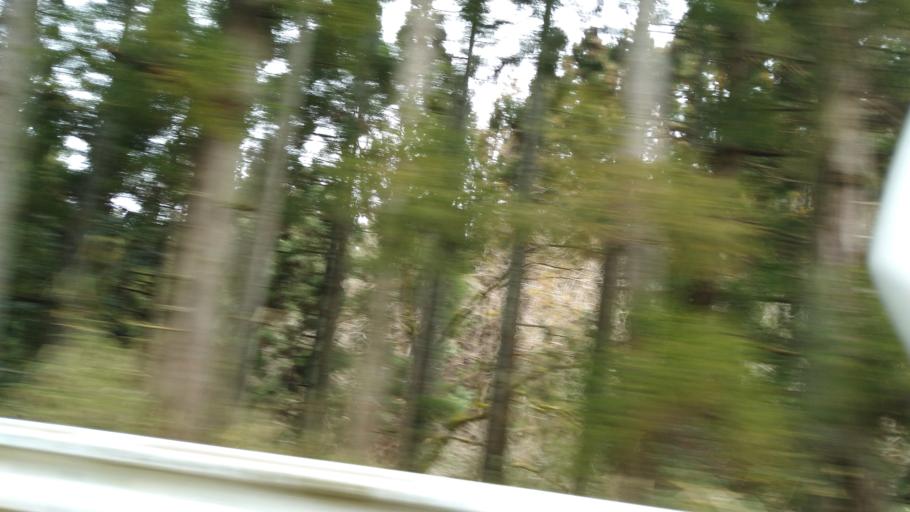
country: JP
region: Kyoto
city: Ayabe
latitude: 35.3179
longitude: 135.3627
